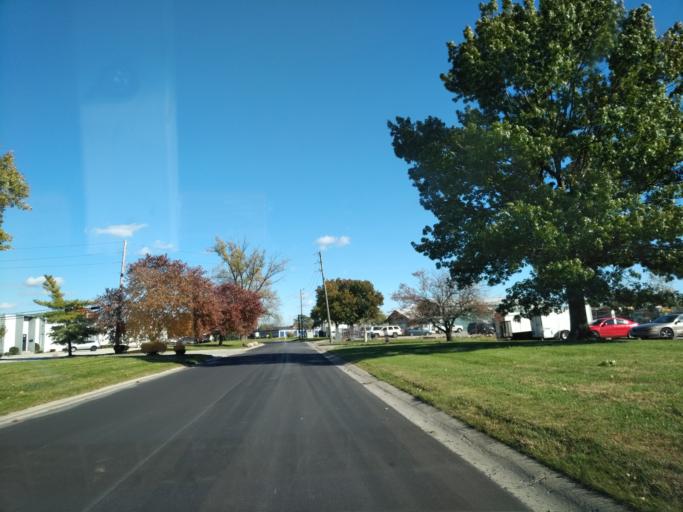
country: US
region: Indiana
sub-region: Marion County
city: Lawrence
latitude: 39.8804
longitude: -86.0761
